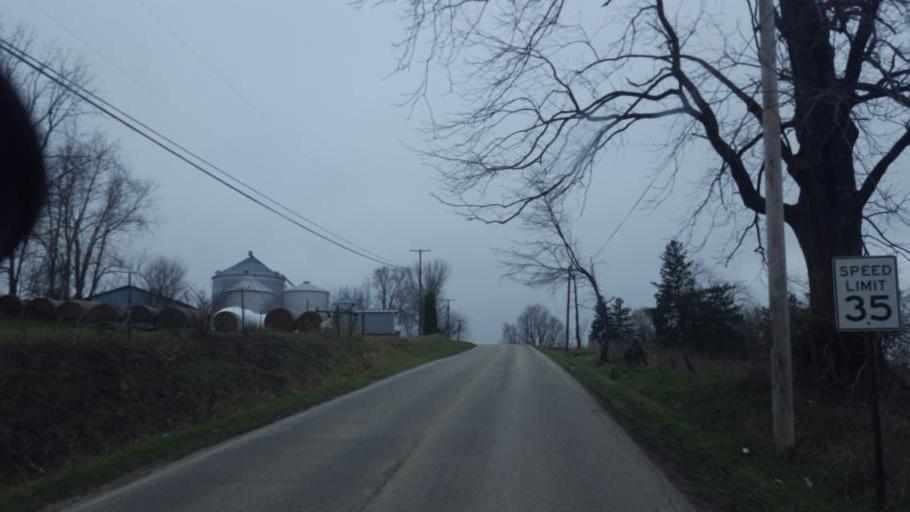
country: US
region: Ohio
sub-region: Richland County
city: Lexington
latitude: 40.6849
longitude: -82.5373
